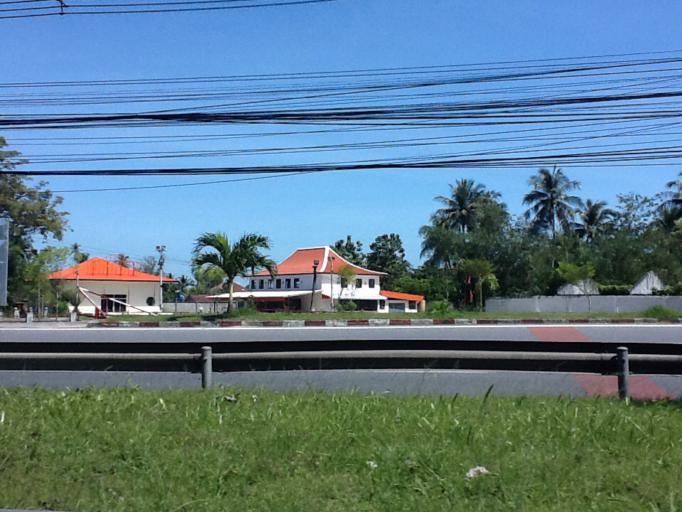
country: TH
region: Phuket
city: Ban Ko Kaeo
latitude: 7.9763
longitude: 98.3686
